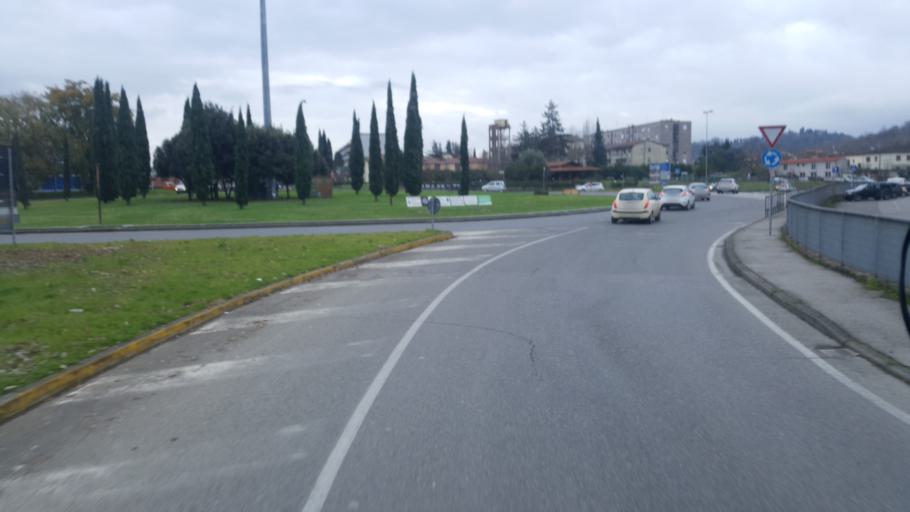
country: IT
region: Tuscany
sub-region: Province of Arezzo
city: Montevarchi
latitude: 43.5355
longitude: 11.5593
